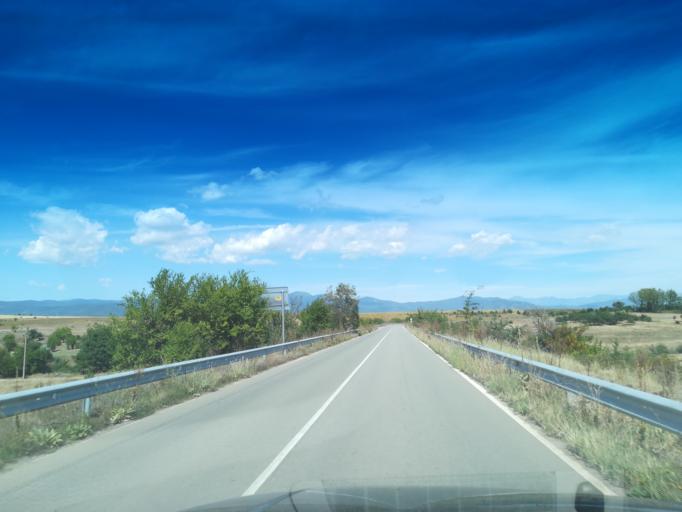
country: BG
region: Plovdiv
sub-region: Obshtina Suedinenie
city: Suedinenie
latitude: 42.4150
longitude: 24.5143
